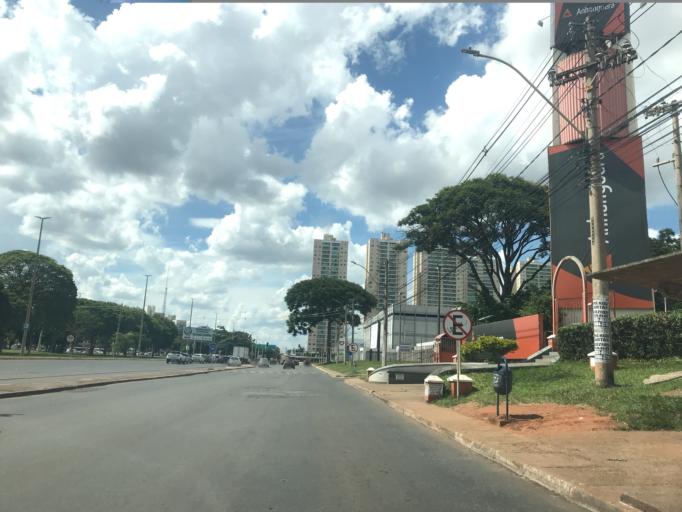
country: BR
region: Federal District
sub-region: Brasilia
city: Brasilia
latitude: -15.8384
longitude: -48.0471
